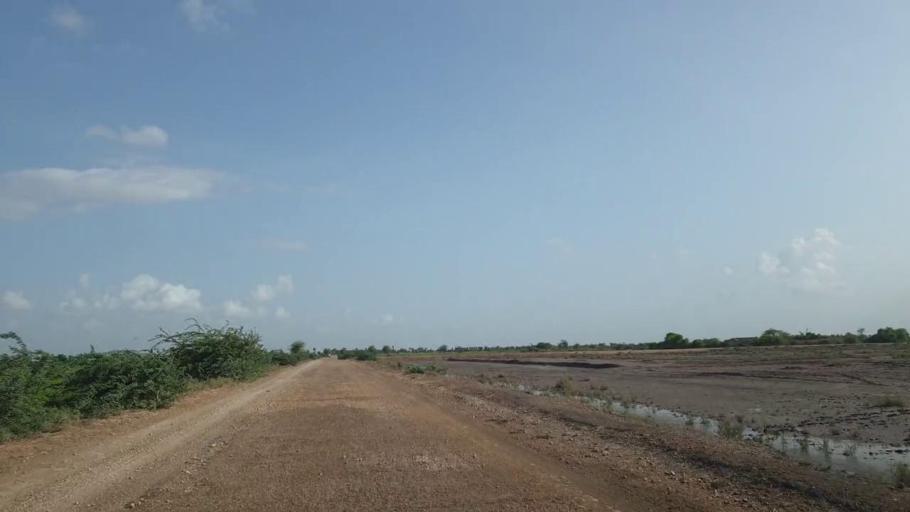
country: PK
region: Sindh
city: Kadhan
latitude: 24.6356
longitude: 69.0960
